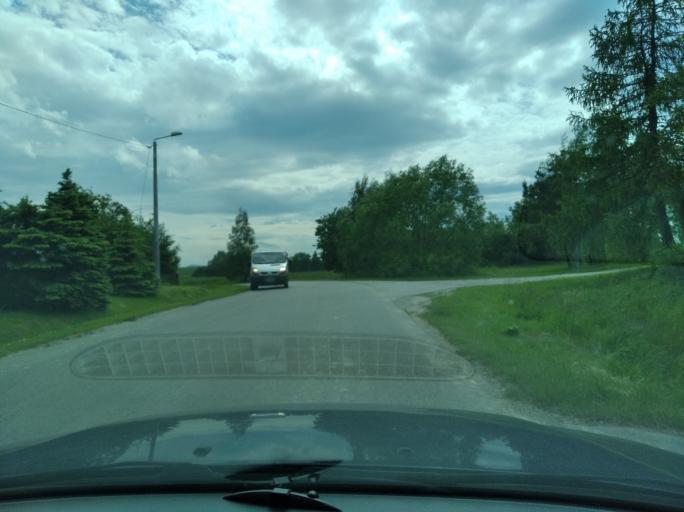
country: PL
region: Subcarpathian Voivodeship
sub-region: Powiat ropczycko-sedziszowski
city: Ropczyce
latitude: 50.0021
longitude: 21.6131
